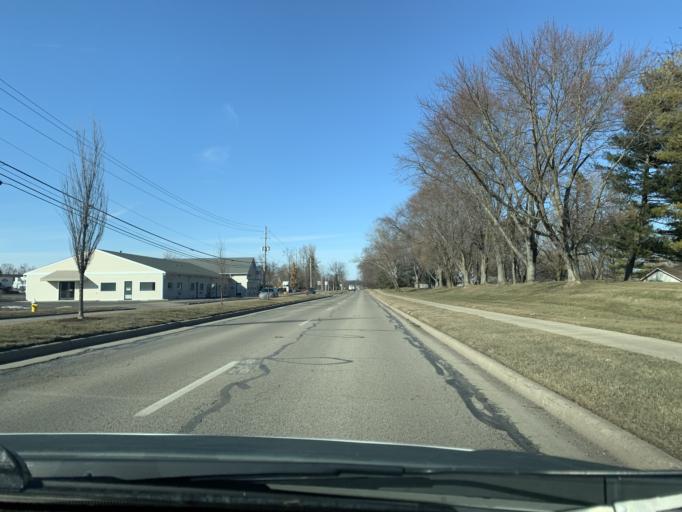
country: US
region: Ohio
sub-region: Montgomery County
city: Centerville
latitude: 39.6297
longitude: -84.1392
